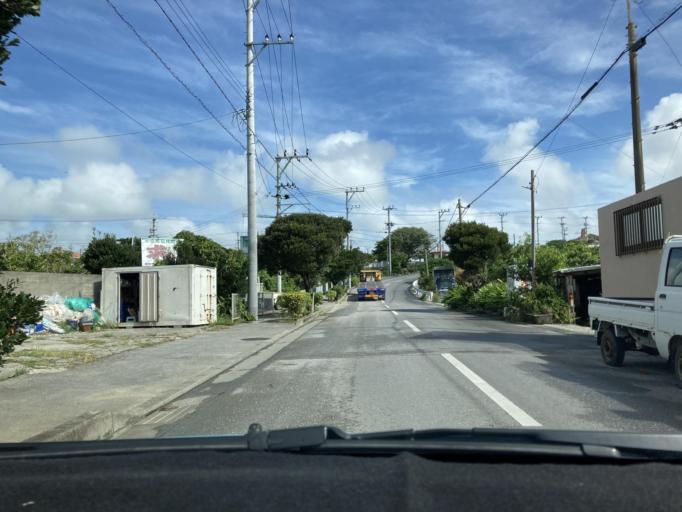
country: JP
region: Okinawa
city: Itoman
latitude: 26.1046
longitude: 127.6627
